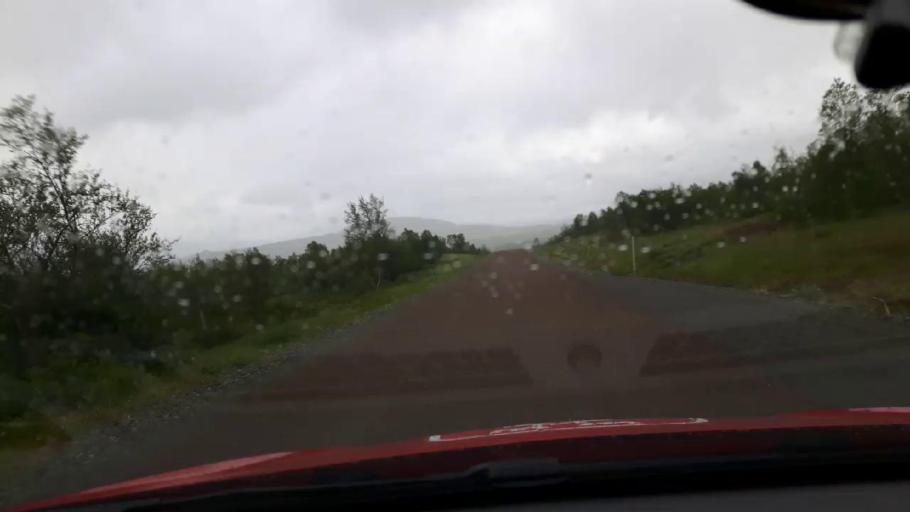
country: NO
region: Nord-Trondelag
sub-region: Meraker
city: Meraker
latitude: 63.1837
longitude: 12.3783
